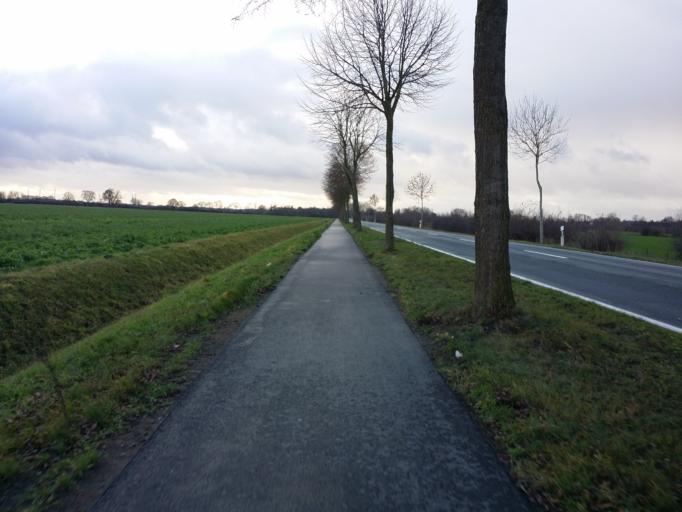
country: DE
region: Lower Saxony
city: Riede
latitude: 52.9975
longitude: 8.8999
